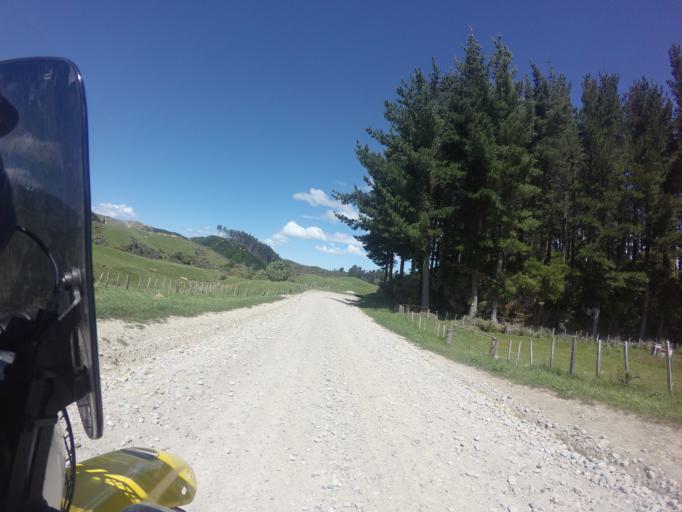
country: NZ
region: Hawke's Bay
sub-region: Wairoa District
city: Wairoa
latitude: -38.9719
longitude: 177.7028
